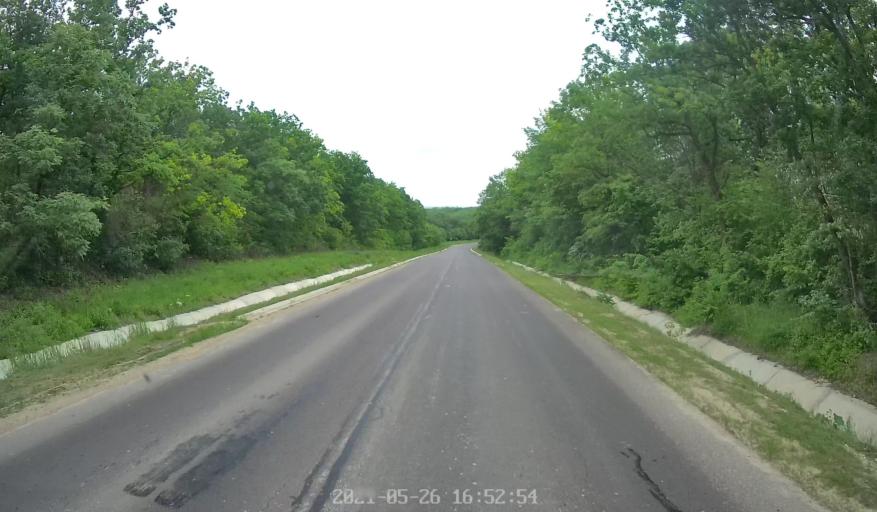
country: MD
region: Hincesti
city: Hincesti
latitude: 46.8594
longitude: 28.5228
